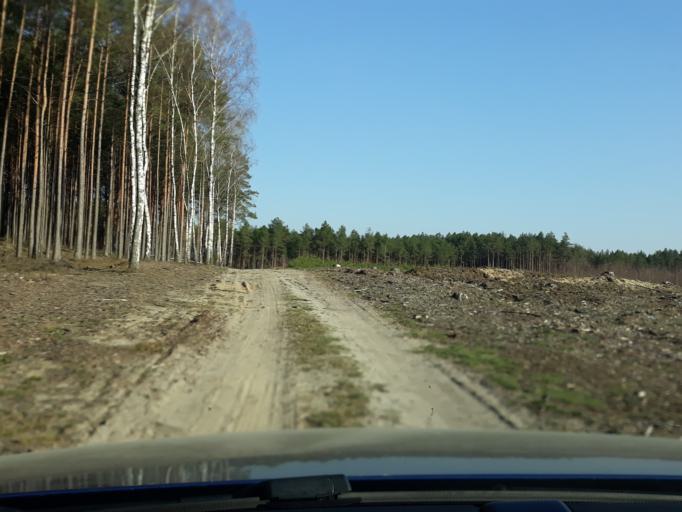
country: PL
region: Pomeranian Voivodeship
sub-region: Powiat bytowski
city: Lipnica
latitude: 53.9141
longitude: 17.4786
